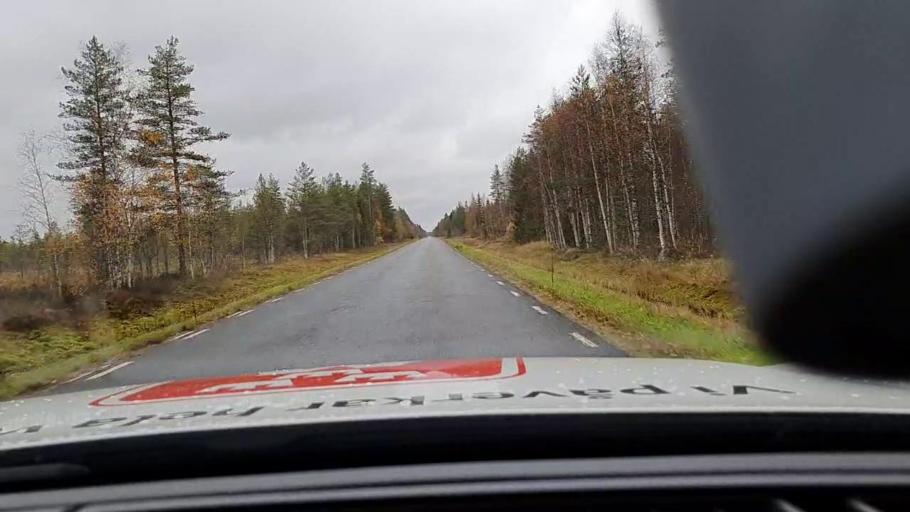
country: SE
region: Norrbotten
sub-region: Haparanda Kommun
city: Haparanda
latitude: 65.9074
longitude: 23.8315
